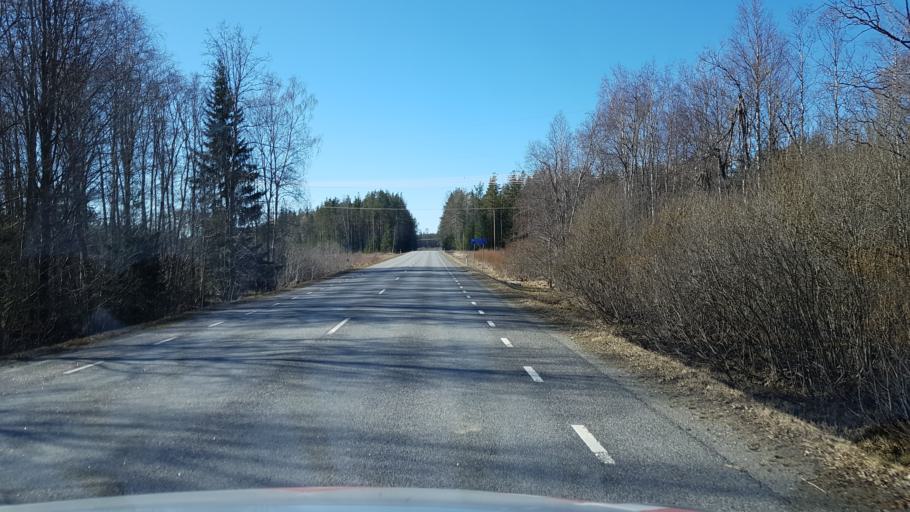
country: EE
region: Laeaene-Virumaa
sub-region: Viru-Nigula vald
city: Kunda
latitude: 59.3654
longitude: 26.6093
